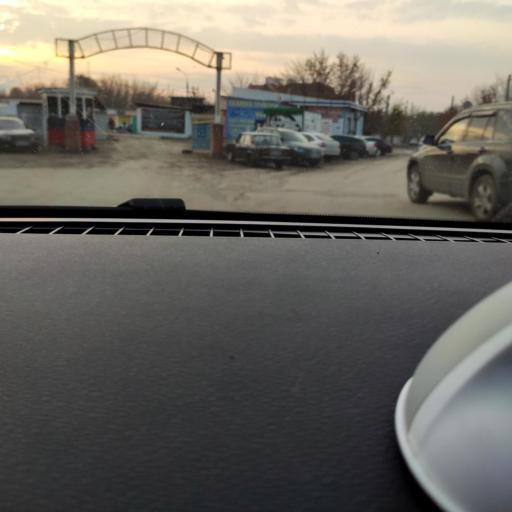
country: RU
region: Samara
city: Samara
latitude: 53.2145
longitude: 50.2597
